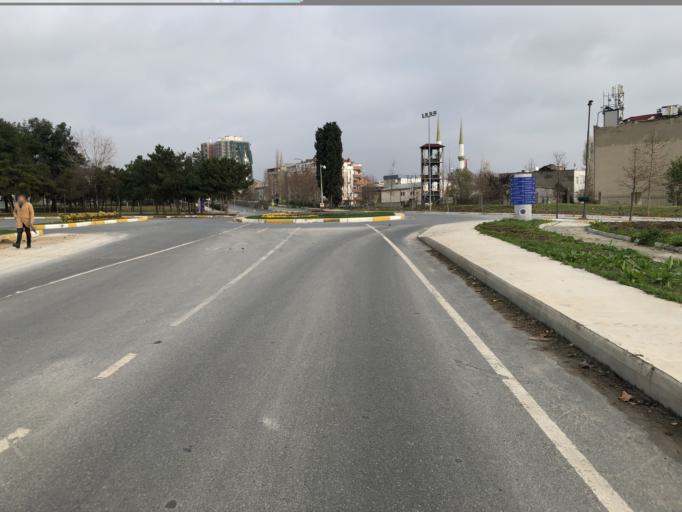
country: TR
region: Istanbul
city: merter keresteciler
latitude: 41.0250
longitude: 28.8939
